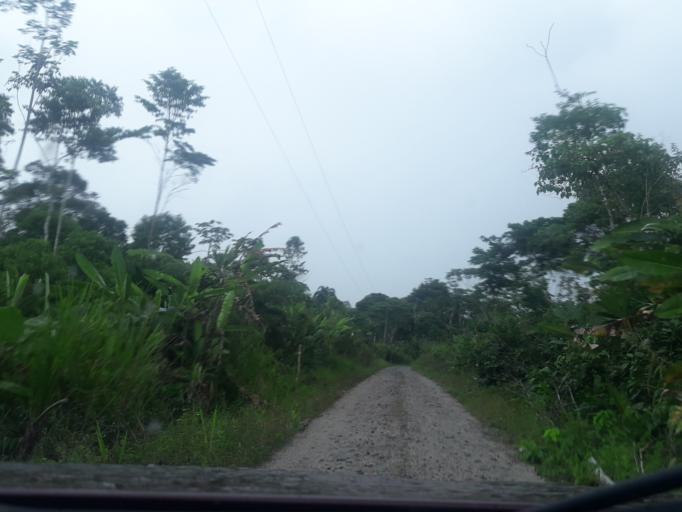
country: EC
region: Napo
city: Tena
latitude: -1.1013
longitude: -77.6869
